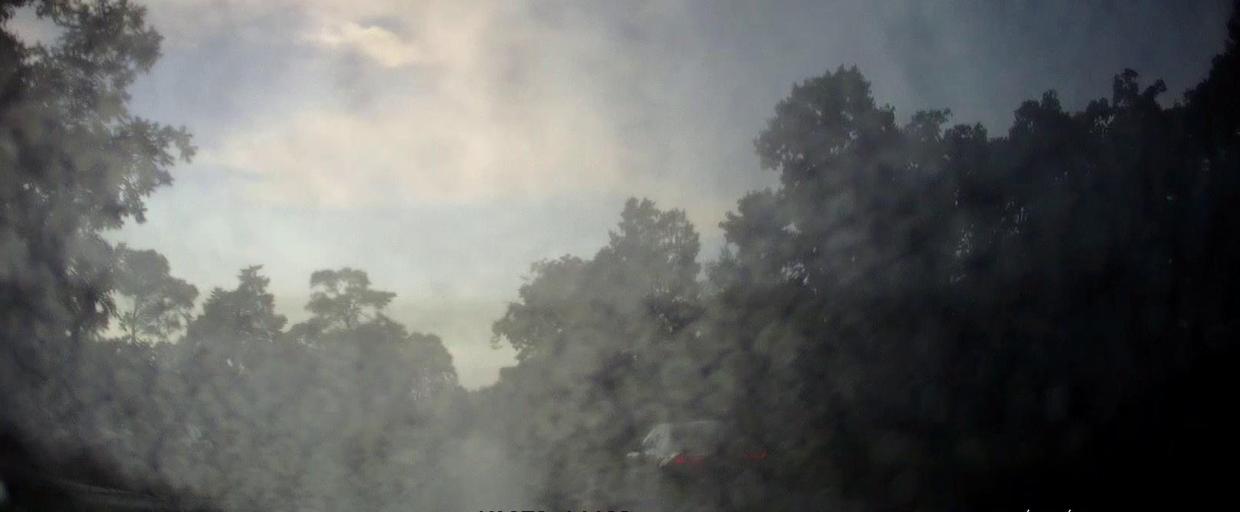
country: US
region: Georgia
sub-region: Dodge County
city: Chester
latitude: 32.5576
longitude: -83.1502
